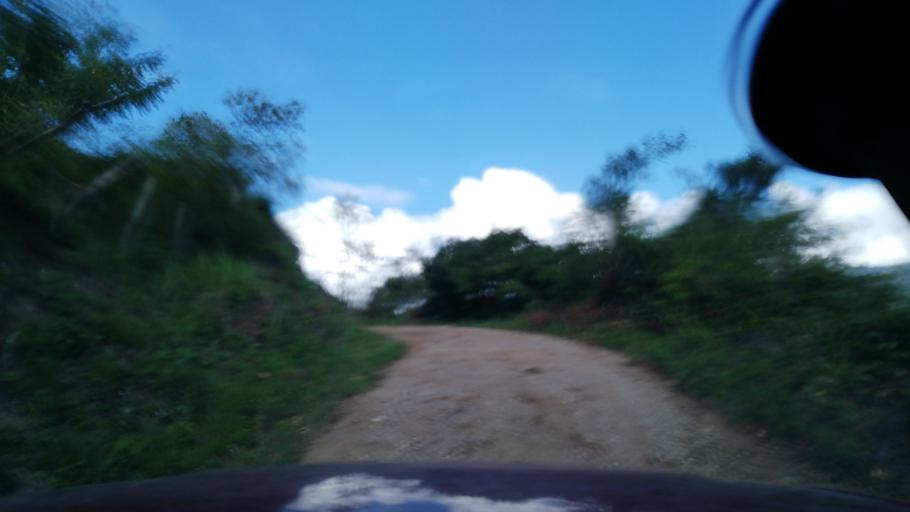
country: CO
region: Cundinamarca
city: Quipile
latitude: 4.7535
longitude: -74.6165
